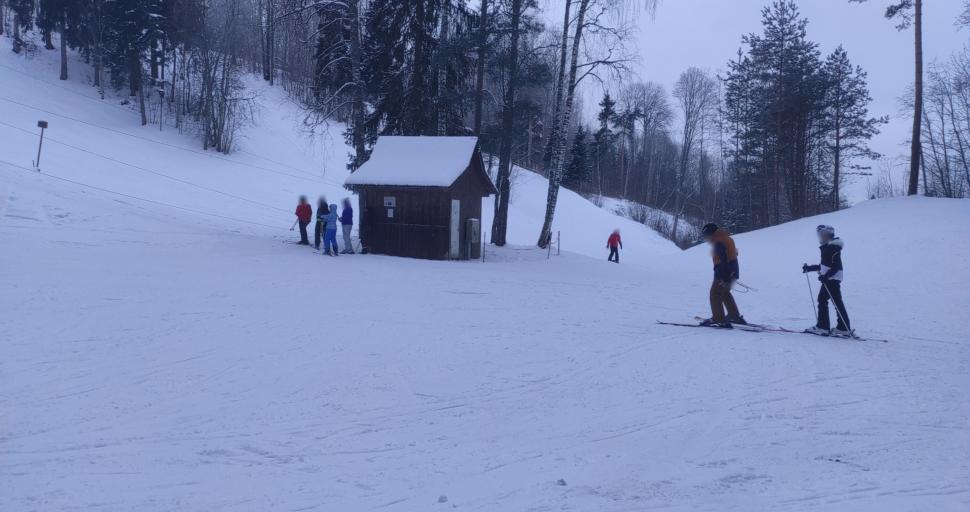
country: LV
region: Plavinu
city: Plavinas
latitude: 56.6542
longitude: 25.7390
